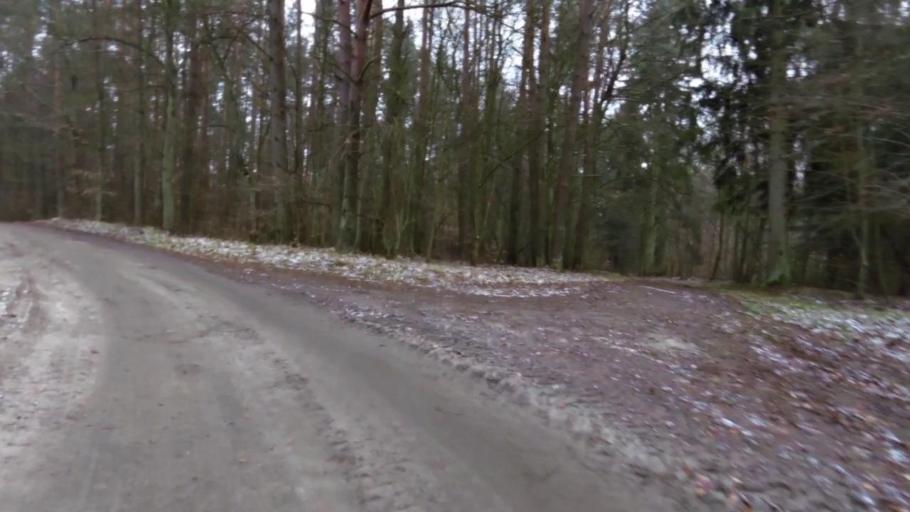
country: PL
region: West Pomeranian Voivodeship
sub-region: Powiat walecki
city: Walcz
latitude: 53.3057
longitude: 16.4695
